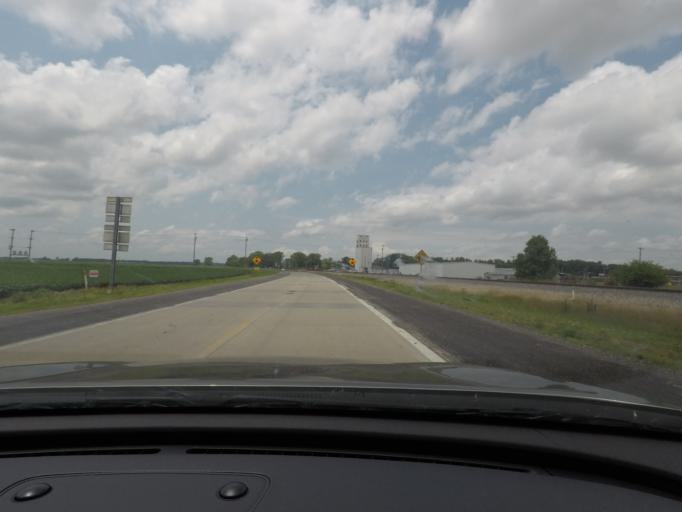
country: US
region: Missouri
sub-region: Carroll County
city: Carrollton
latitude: 39.3400
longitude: -93.4939
